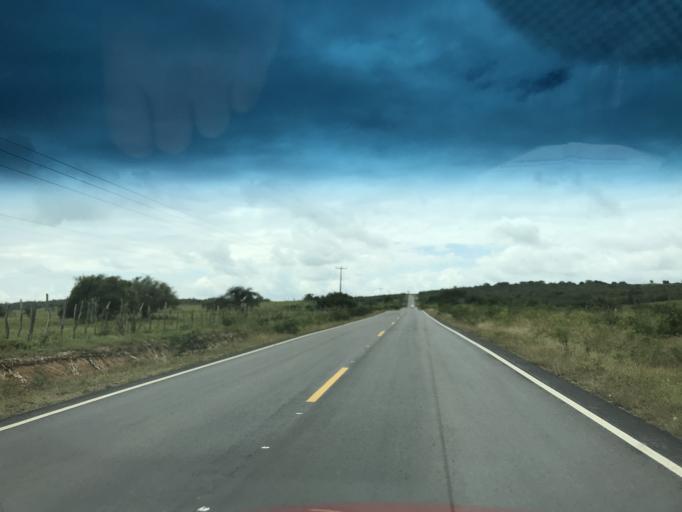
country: BR
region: Bahia
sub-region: Conceicao Do Almeida
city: Conceicao do Almeida
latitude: -12.6724
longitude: -39.2920
